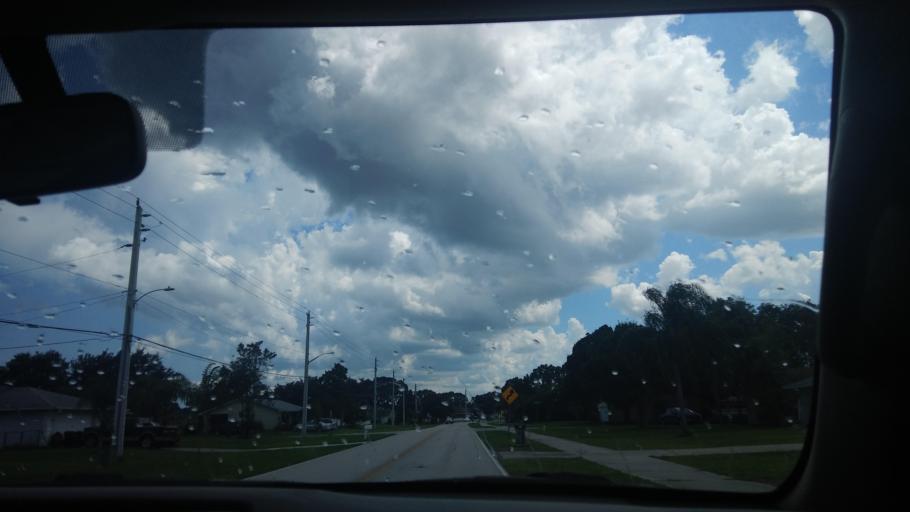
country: US
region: Florida
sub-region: Brevard County
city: Palm Bay
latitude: 28.0073
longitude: -80.6457
